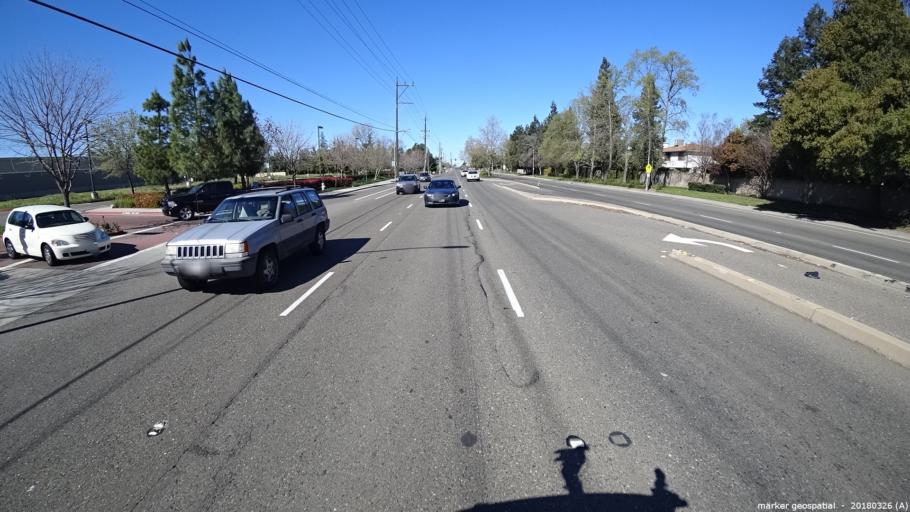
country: US
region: California
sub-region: Sacramento County
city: Vineyard
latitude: 38.4525
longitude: -121.3758
